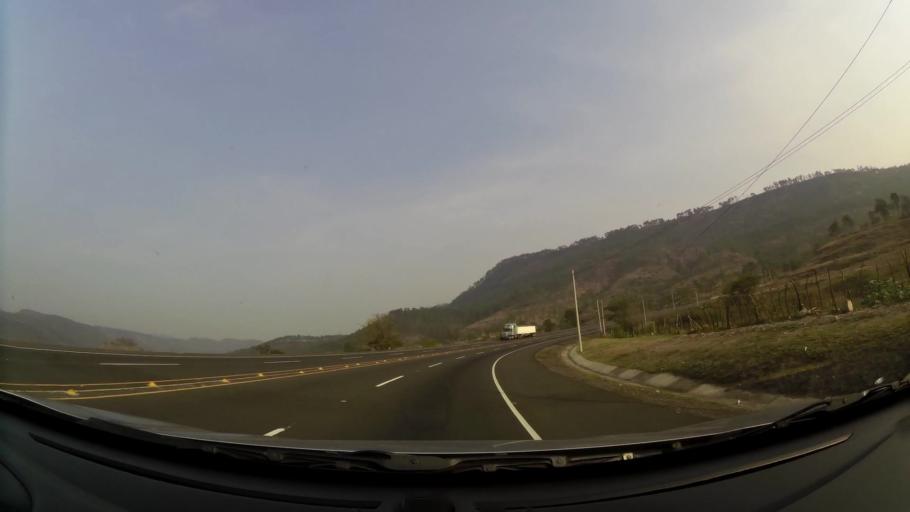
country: HN
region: Francisco Morazan
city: Zambrano
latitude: 14.2329
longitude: -87.3875
